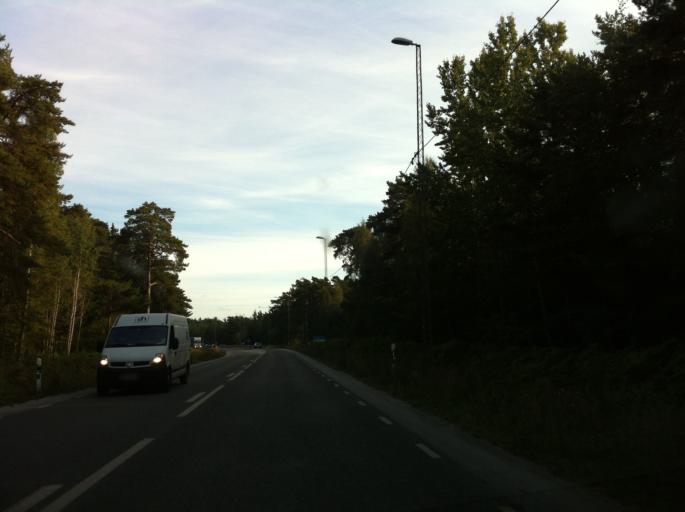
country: SE
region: Gotland
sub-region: Gotland
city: Visby
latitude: 57.6127
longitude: 18.2904
